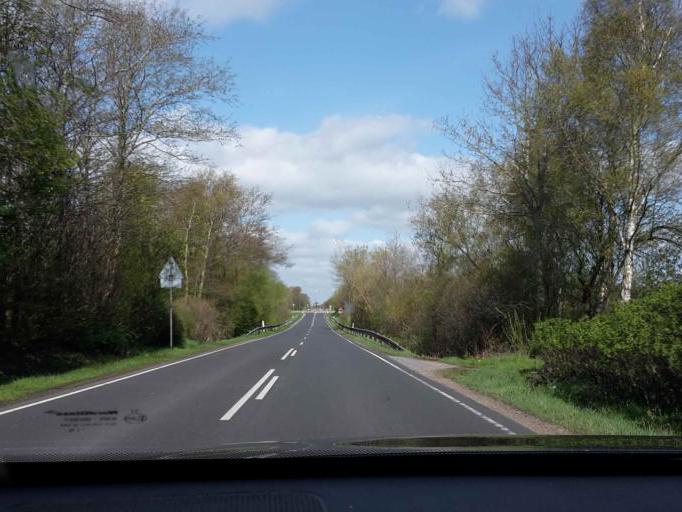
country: DK
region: South Denmark
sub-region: Varde Kommune
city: Olgod
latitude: 55.7067
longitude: 8.7566
